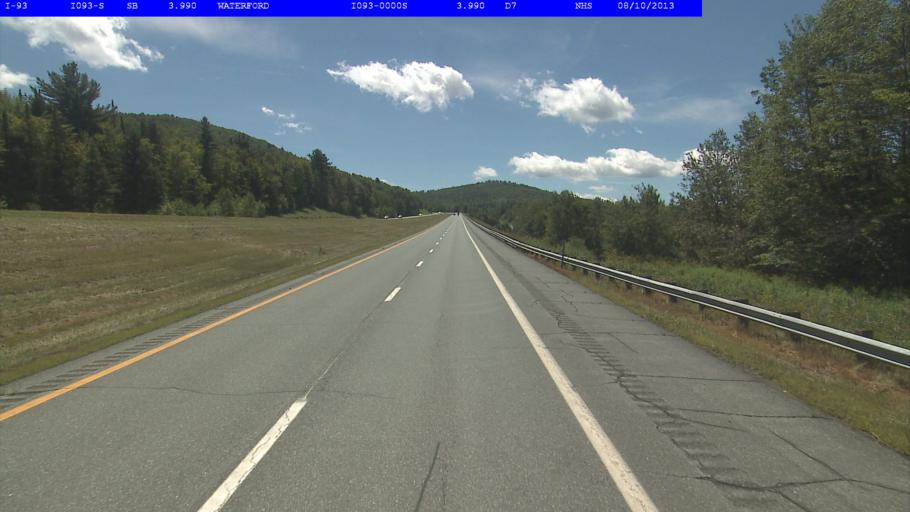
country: US
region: Vermont
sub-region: Caledonia County
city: Saint Johnsbury
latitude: 44.3933
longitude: -71.9213
